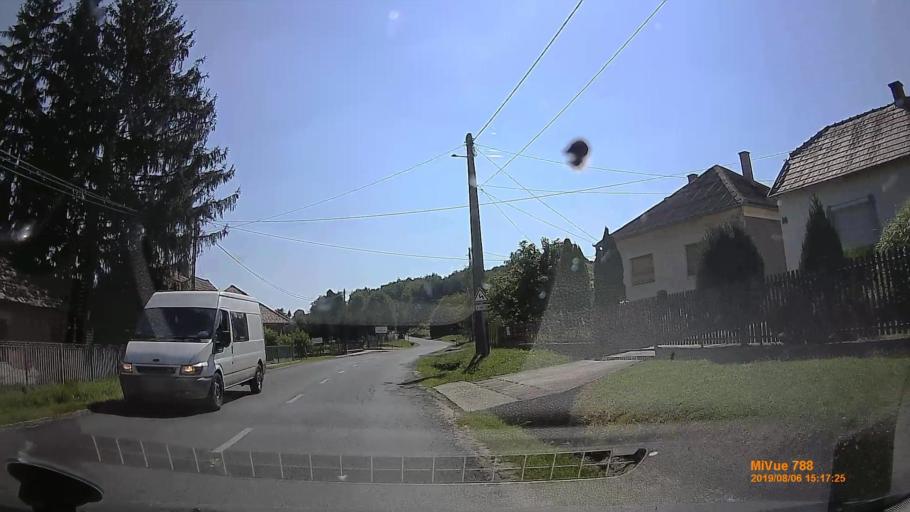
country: HU
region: Zala
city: Murakeresztur
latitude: 46.3154
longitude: 16.9647
